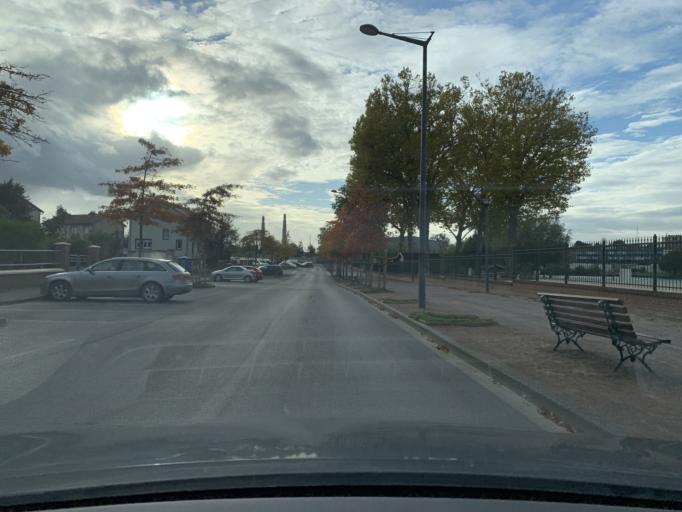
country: FR
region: Picardie
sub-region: Departement de l'Aisne
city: Harly
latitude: 49.8419
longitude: 3.3013
